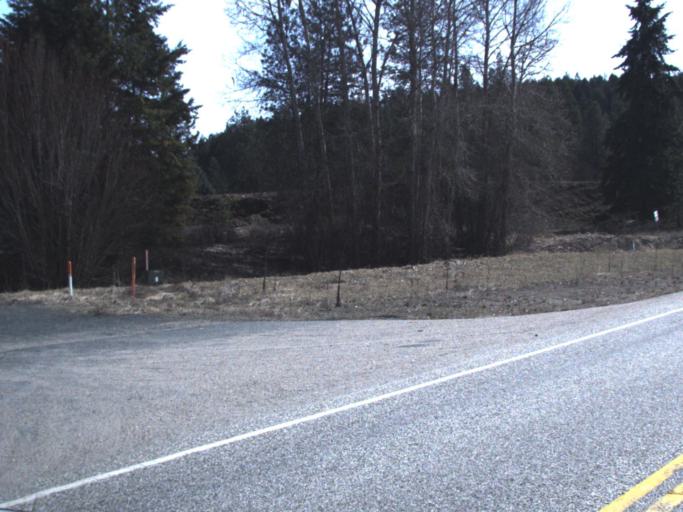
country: US
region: Washington
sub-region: Stevens County
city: Colville
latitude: 48.5134
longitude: -117.7773
